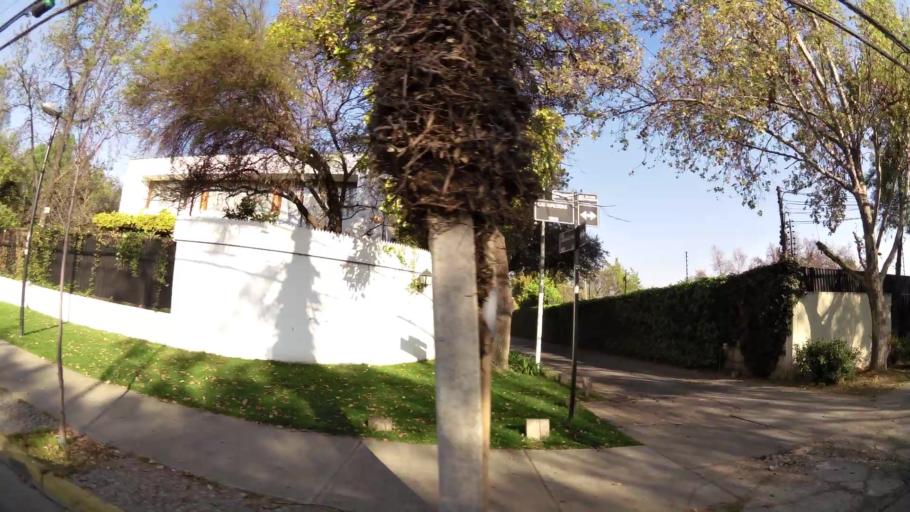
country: CL
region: Santiago Metropolitan
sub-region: Provincia de Santiago
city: Villa Presidente Frei, Nunoa, Santiago, Chile
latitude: -33.3785
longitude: -70.5322
